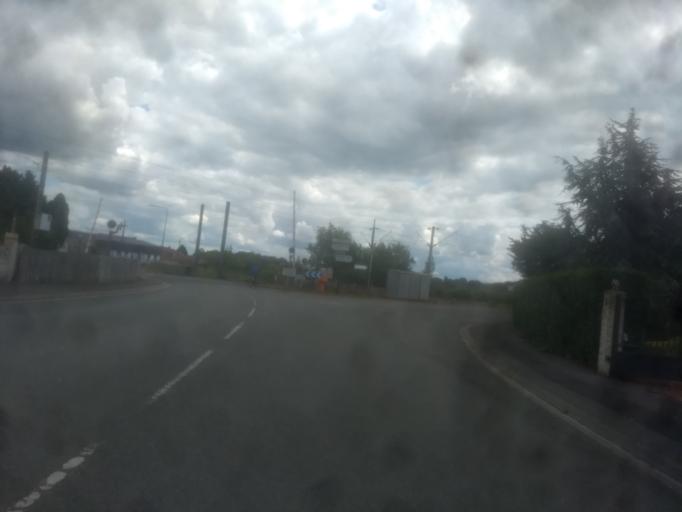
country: FR
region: Nord-Pas-de-Calais
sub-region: Departement du Pas-de-Calais
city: Agny
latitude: 50.2167
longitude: 2.7677
